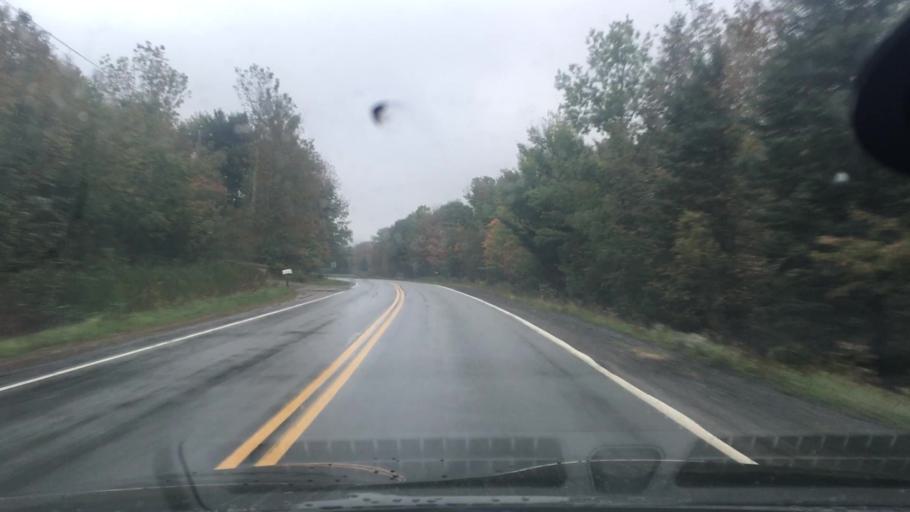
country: CA
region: Nova Scotia
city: Windsor
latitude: 44.8434
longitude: -64.2285
